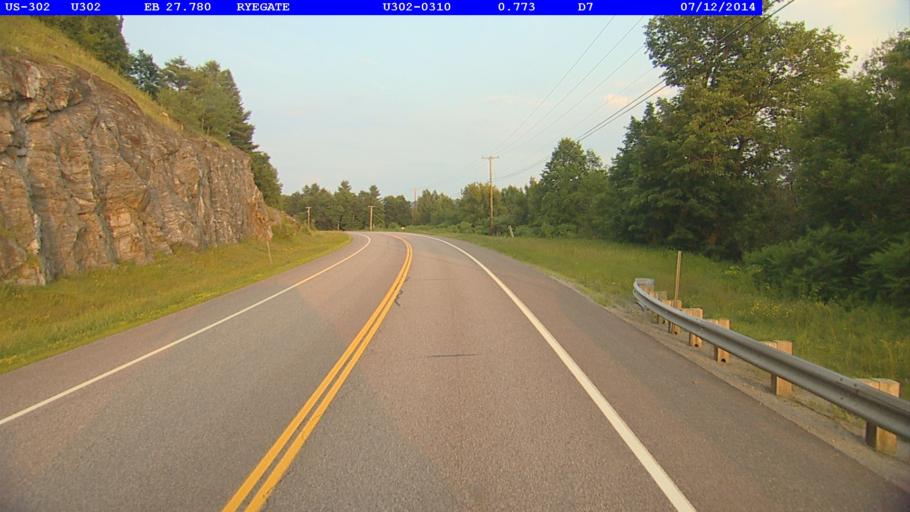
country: US
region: New Hampshire
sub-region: Grafton County
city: Woodsville
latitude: 44.1982
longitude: -72.1590
